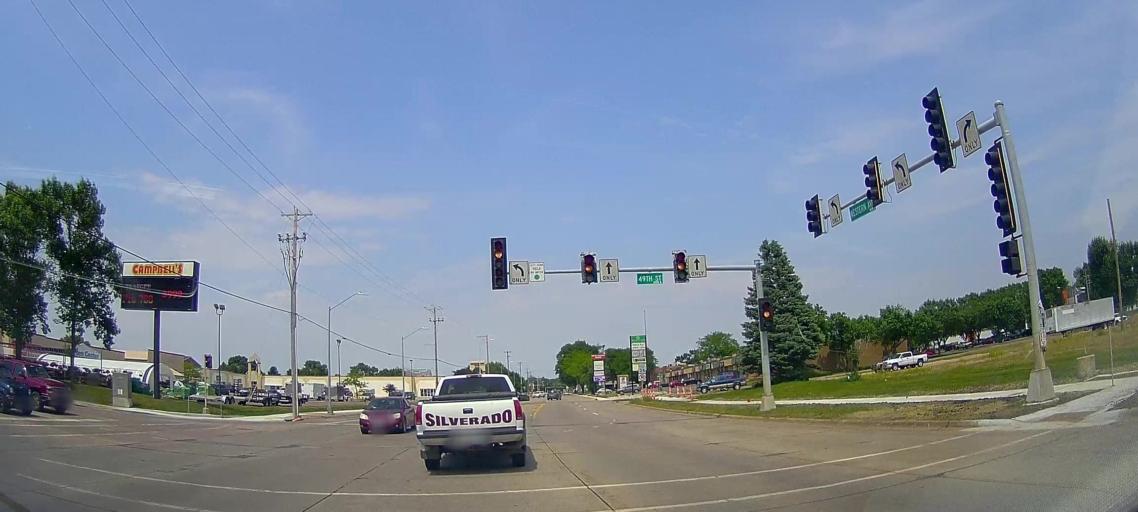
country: US
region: South Dakota
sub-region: Minnehaha County
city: Sioux Falls
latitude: 43.5083
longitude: -96.7511
